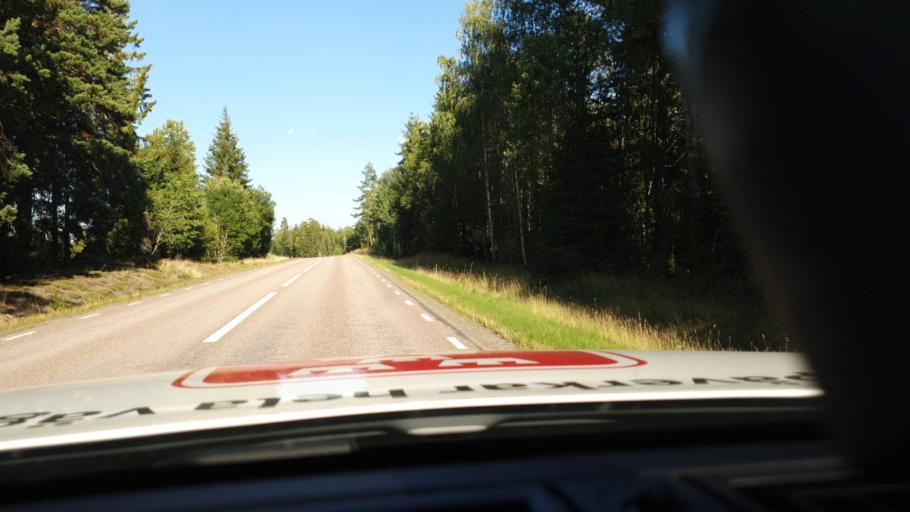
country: SE
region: OEstergoetland
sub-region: Ydre Kommun
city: OEsterbymo
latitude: 57.8020
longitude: 15.1795
